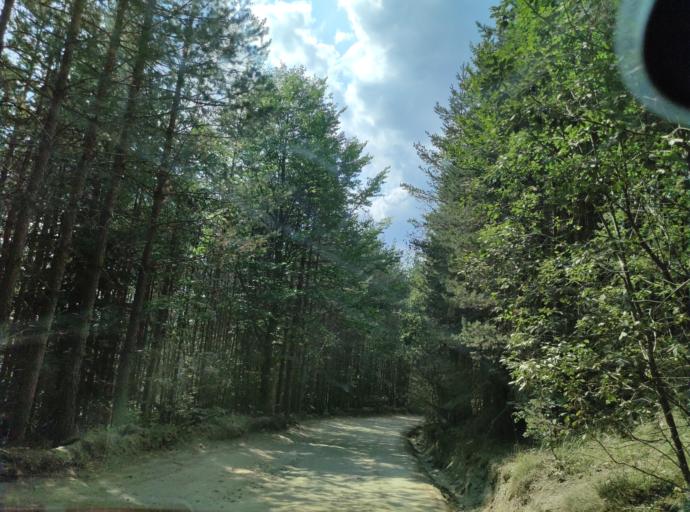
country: BG
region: Blagoevgrad
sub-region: Obshtina Belitsa
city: Belitsa
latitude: 42.0257
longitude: 23.5802
